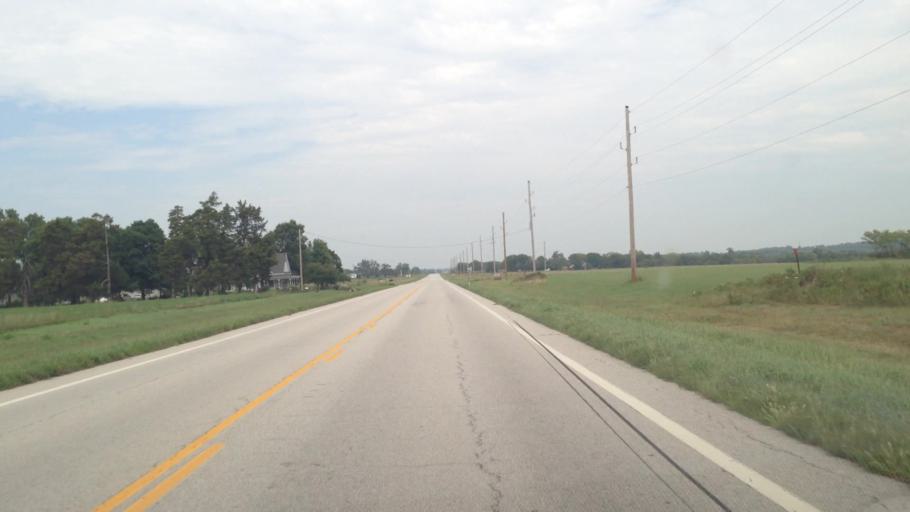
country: US
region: Kansas
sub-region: Allen County
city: Iola
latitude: 37.9773
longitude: -95.1703
